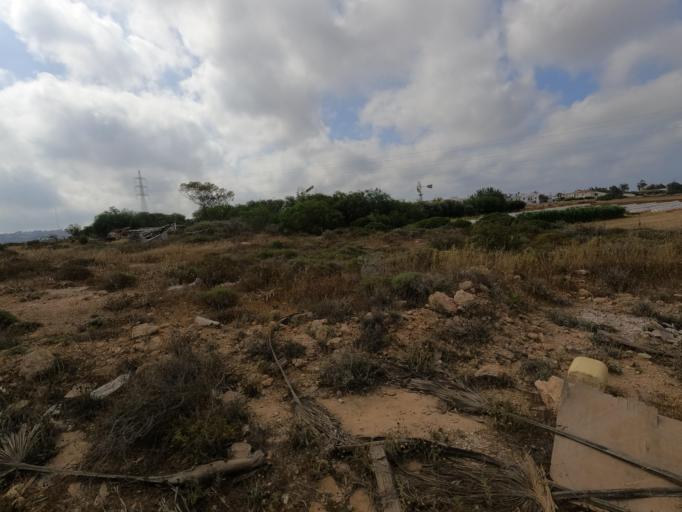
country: CY
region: Ammochostos
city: Ayia Napa
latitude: 35.0083
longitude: 34.0078
